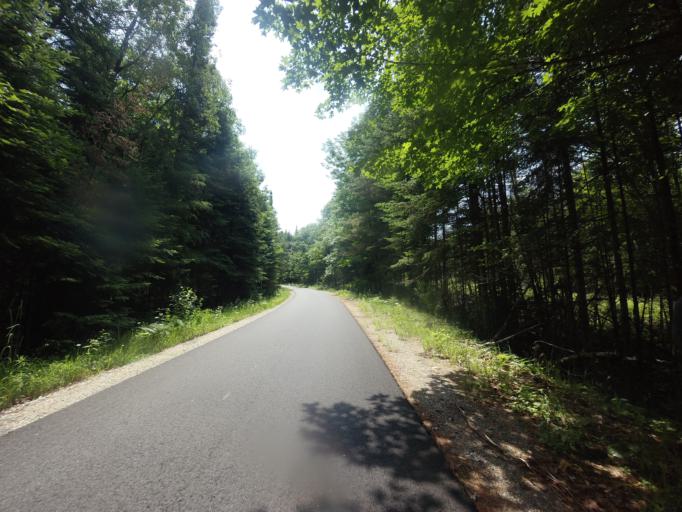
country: CA
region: Quebec
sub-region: Outaouais
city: Maniwaki
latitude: 46.1439
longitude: -76.0410
